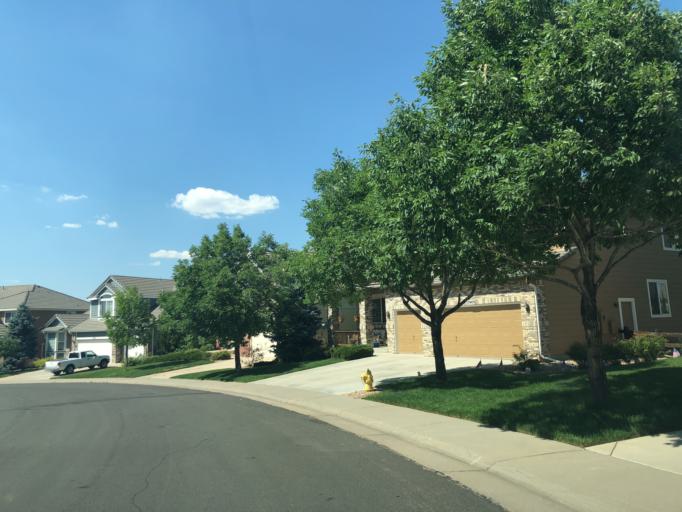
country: US
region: Colorado
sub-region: Arapahoe County
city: Dove Valley
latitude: 39.6083
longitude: -104.7853
